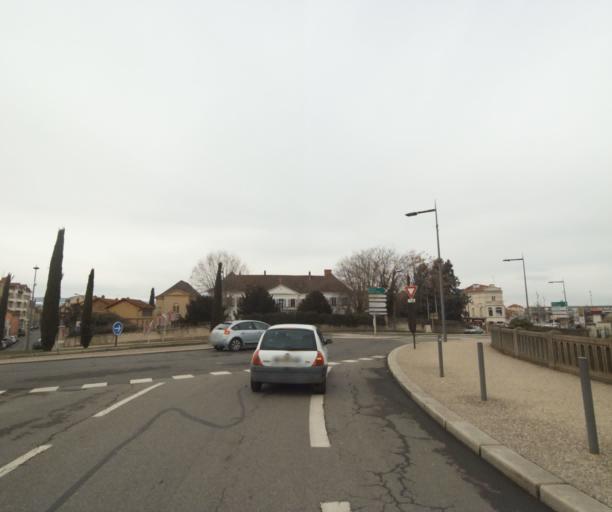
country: FR
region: Rhone-Alpes
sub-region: Departement de la Loire
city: Roanne
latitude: 46.0365
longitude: 4.0645
